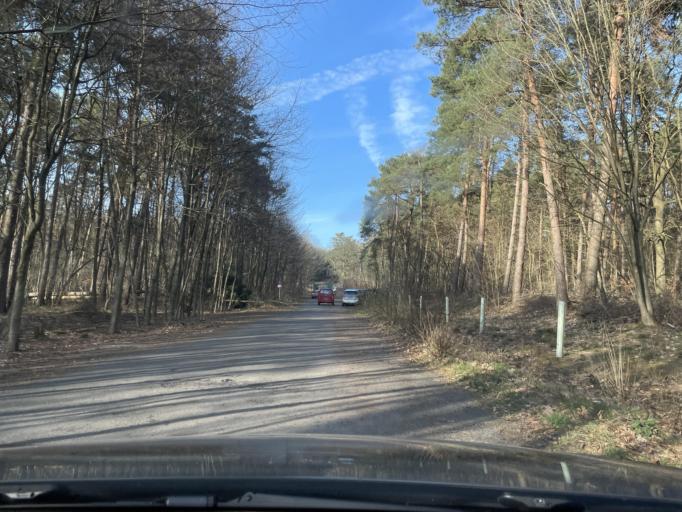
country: NL
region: Limburg
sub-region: Gemeente Beesel
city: Offenbeek
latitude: 51.2345
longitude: 6.1163
